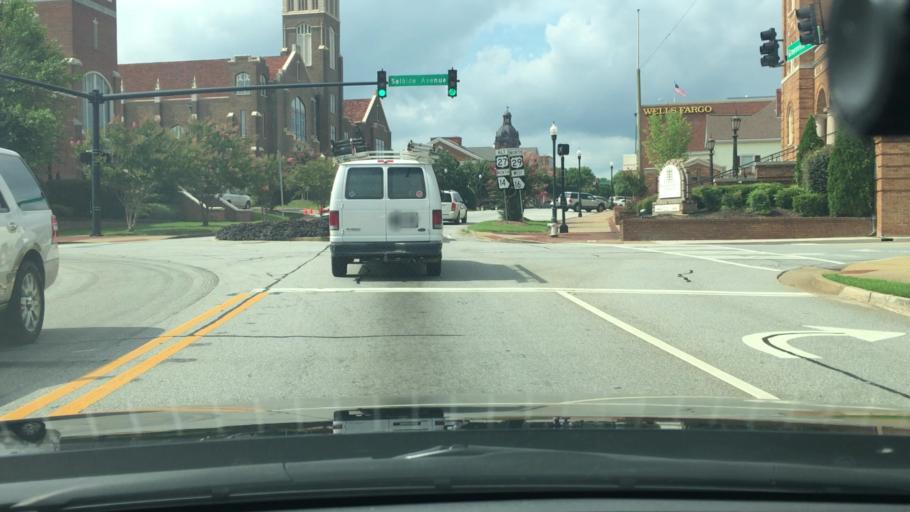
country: US
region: Georgia
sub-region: Coweta County
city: Newnan
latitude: 33.3719
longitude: -84.7997
